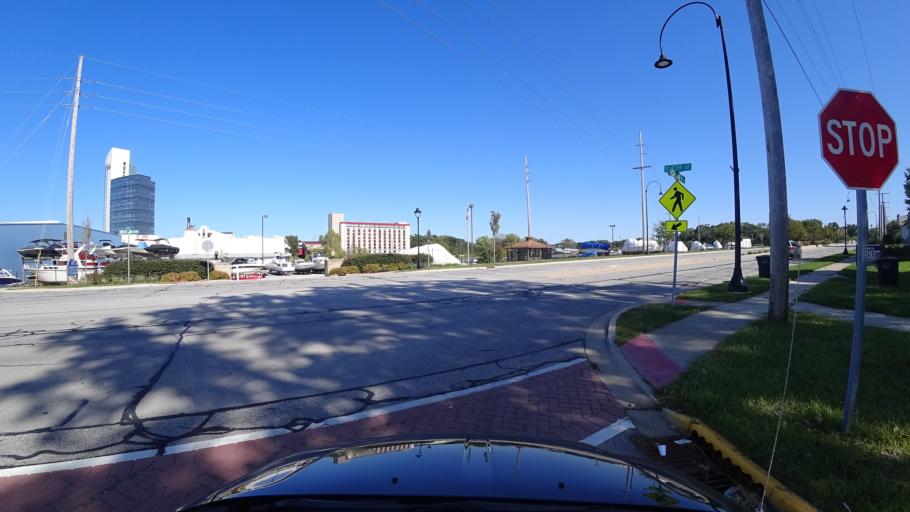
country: US
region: Indiana
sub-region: LaPorte County
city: Michigan City
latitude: 41.7168
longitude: -86.8943
